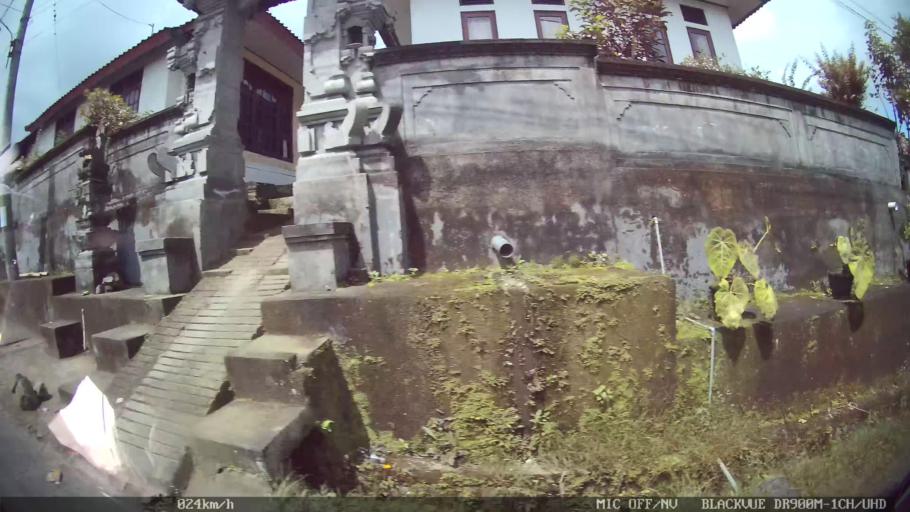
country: ID
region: Bali
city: Banjar Susut Kaja
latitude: -8.4389
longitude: 115.3304
